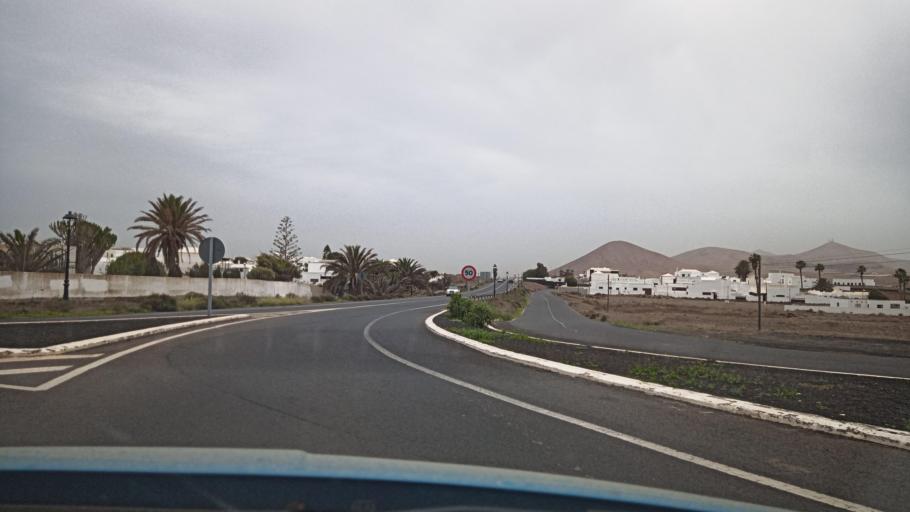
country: ES
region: Canary Islands
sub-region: Provincia de Las Palmas
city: Nazaret
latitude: 29.0191
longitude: -13.5394
